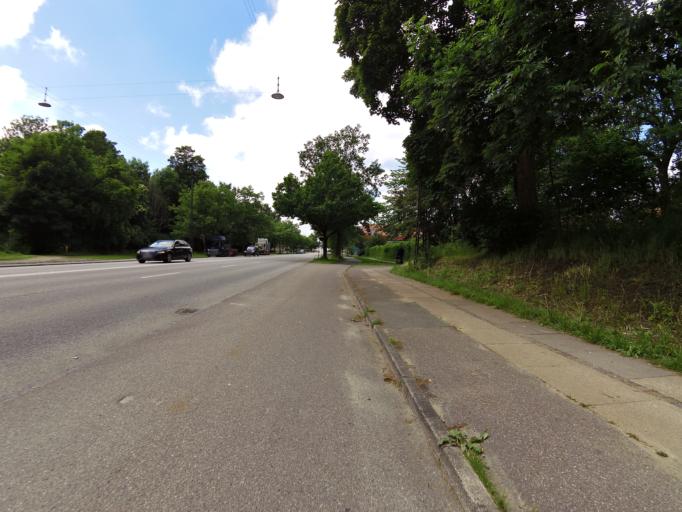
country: DK
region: Capital Region
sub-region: Herlev Kommune
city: Herlev
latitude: 55.7144
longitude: 12.4647
